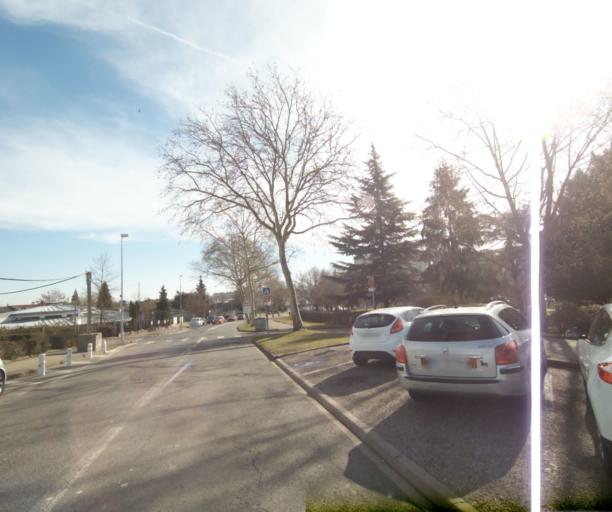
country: FR
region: Lorraine
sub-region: Departement de Meurthe-et-Moselle
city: Vandoeuvre-les-Nancy
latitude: 48.6669
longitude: 6.1801
